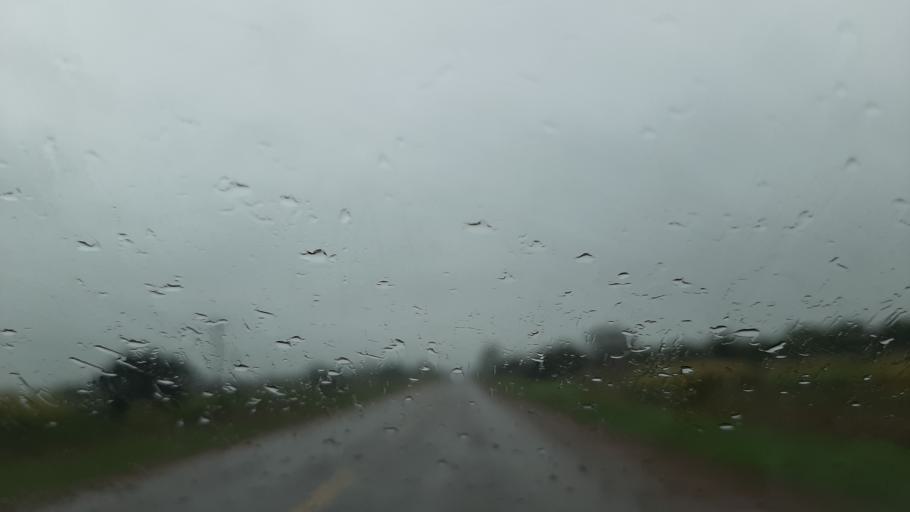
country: BO
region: Santa Cruz
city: Okinawa Numero Uno
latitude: -16.8605
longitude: -62.6107
